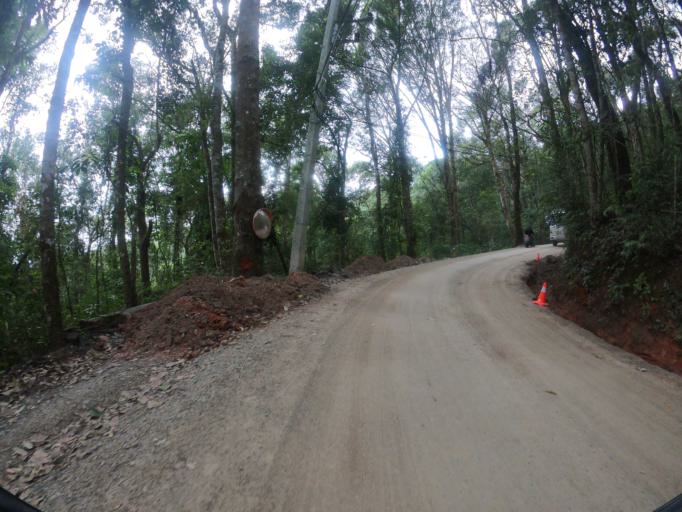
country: TH
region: Chiang Mai
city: Chiang Mai
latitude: 18.8133
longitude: 98.8905
